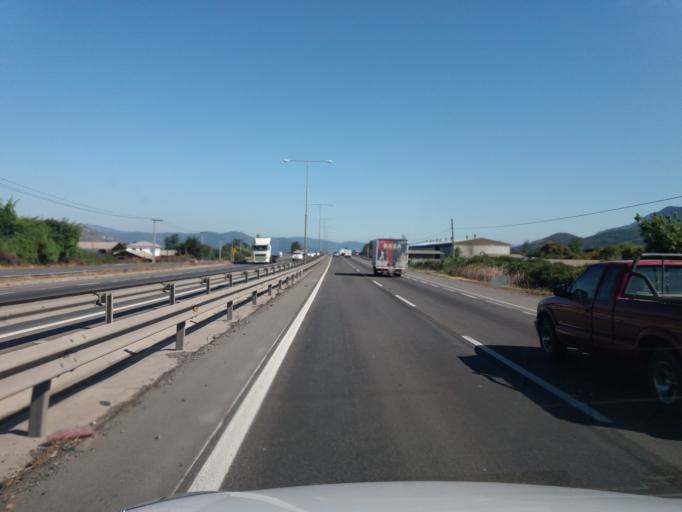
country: CL
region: Valparaiso
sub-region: Provincia de Quillota
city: Hacienda La Calera
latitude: -32.8170
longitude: -71.1420
